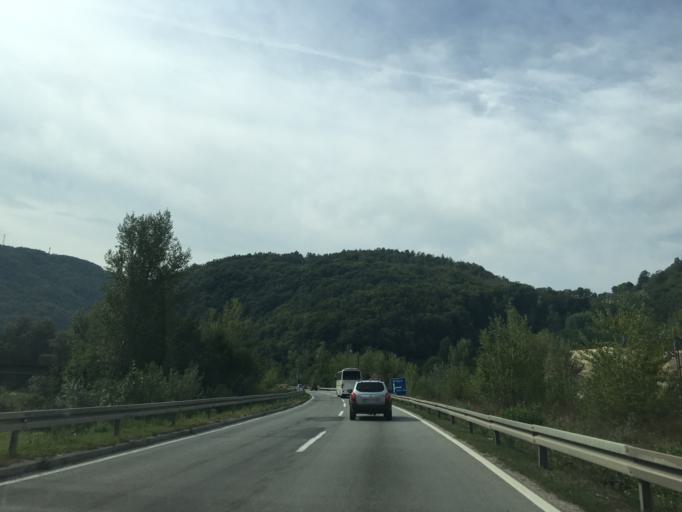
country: RS
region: Central Serbia
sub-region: Moravicki Okrug
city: Lucani
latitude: 43.8927
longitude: 20.1207
